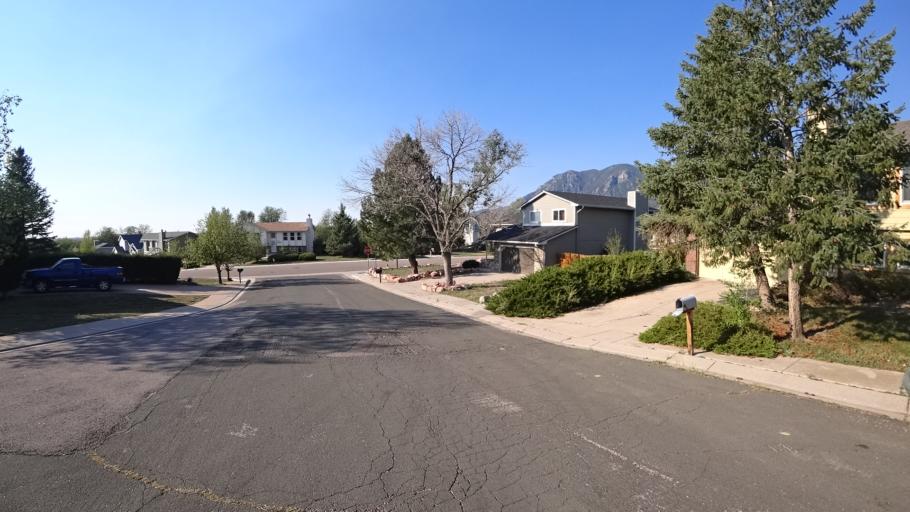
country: US
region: Colorado
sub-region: El Paso County
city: Stratmoor
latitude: 38.7801
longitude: -104.8095
